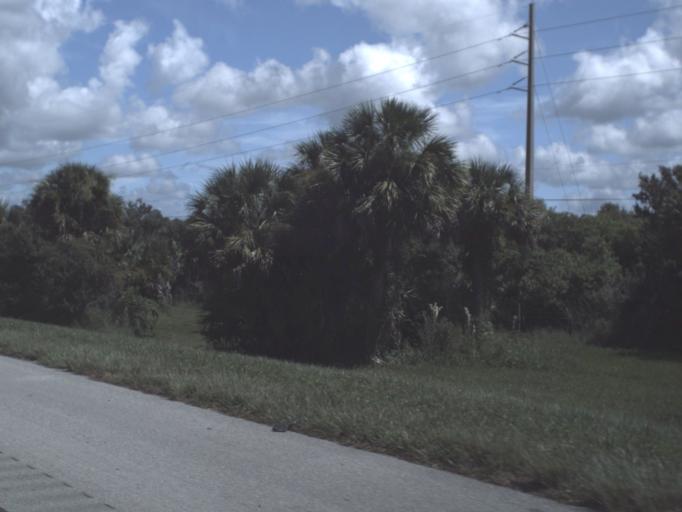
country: US
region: Florida
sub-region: Sarasota County
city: Lake Sarasota
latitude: 27.2514
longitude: -82.4492
